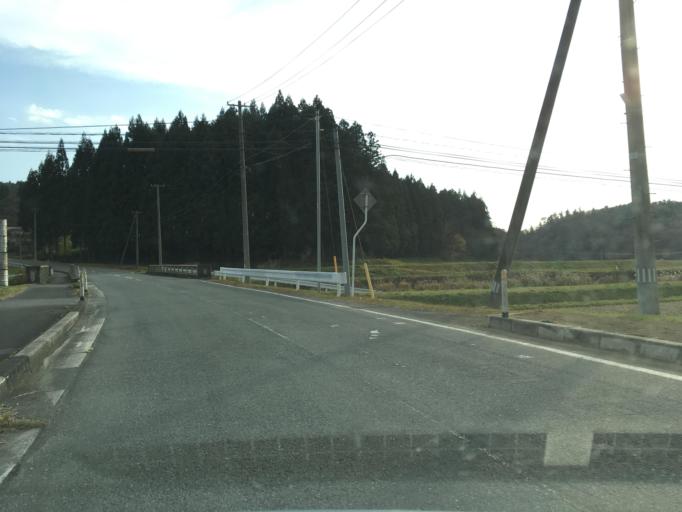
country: JP
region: Iwate
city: Mizusawa
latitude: 39.0411
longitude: 141.3454
